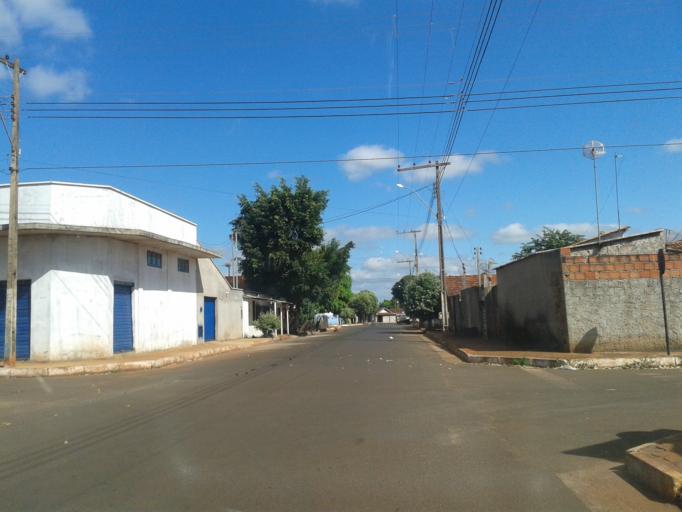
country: BR
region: Minas Gerais
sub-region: Centralina
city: Centralina
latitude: -18.5813
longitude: -49.2037
